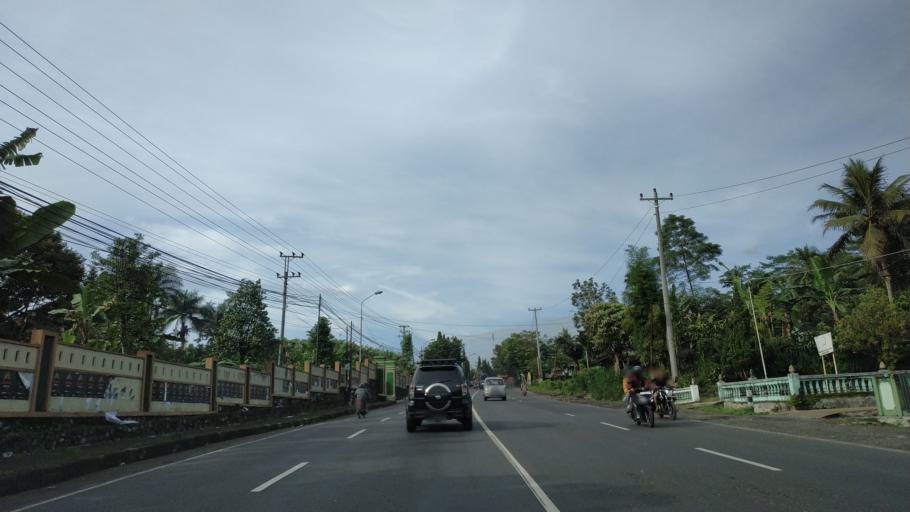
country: ID
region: Central Java
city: Salatiga
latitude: -7.3869
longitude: 110.5150
